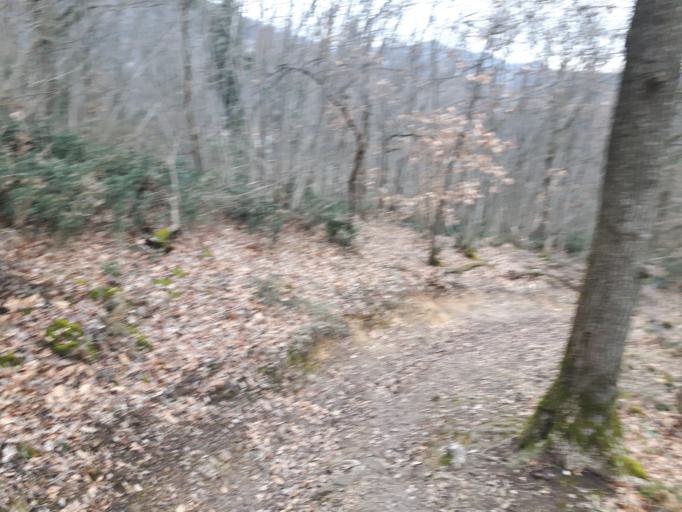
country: IT
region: Veneto
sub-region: Provincia di Padova
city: Arqua Petrarca
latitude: 45.2766
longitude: 11.7425
